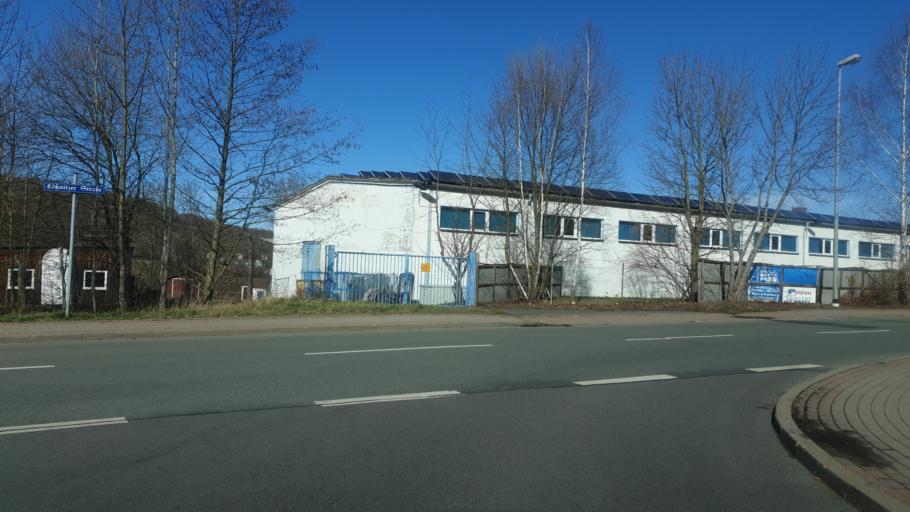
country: DE
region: Saxony
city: Schlema
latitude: 50.6077
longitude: 12.6796
